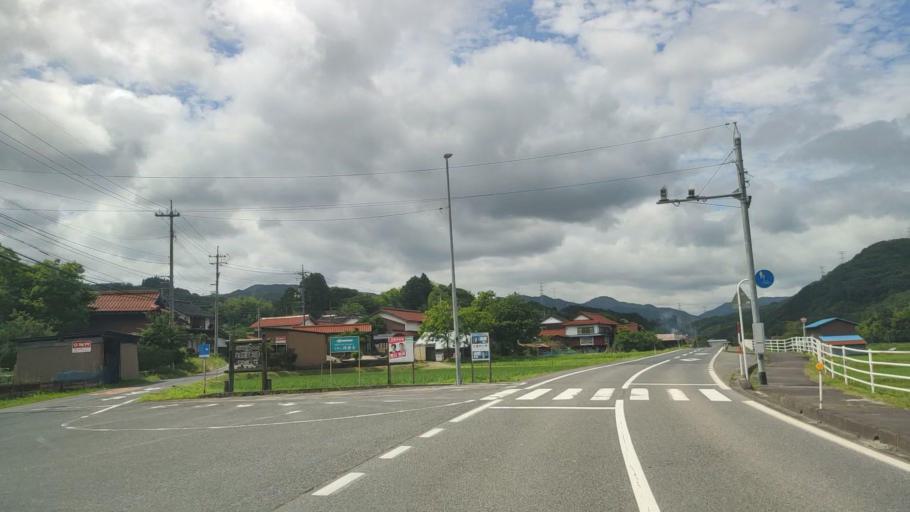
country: JP
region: Tottori
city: Yonago
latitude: 35.3044
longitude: 133.4175
